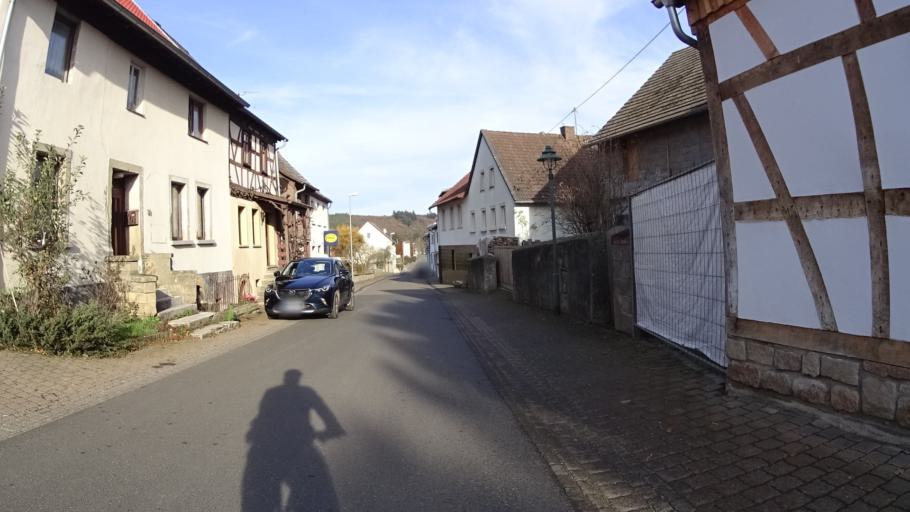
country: DE
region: Rheinland-Pfalz
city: Sien
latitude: 49.6934
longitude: 7.5032
